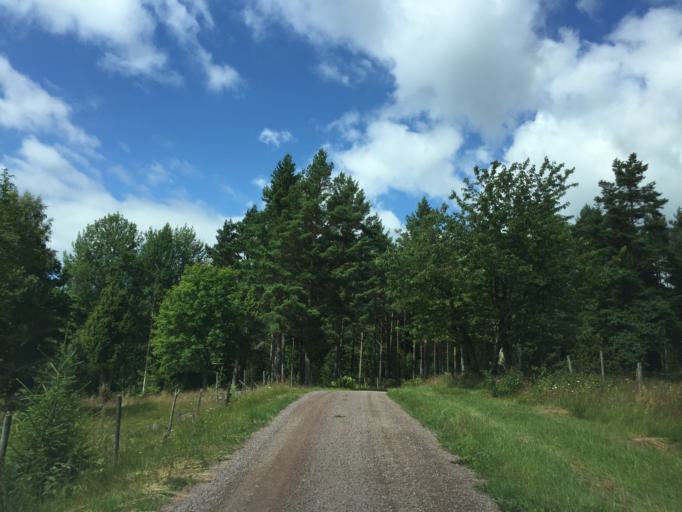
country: SE
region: OEstergoetland
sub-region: Odeshogs Kommun
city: OEdeshoeg
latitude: 58.1784
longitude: 14.6974
